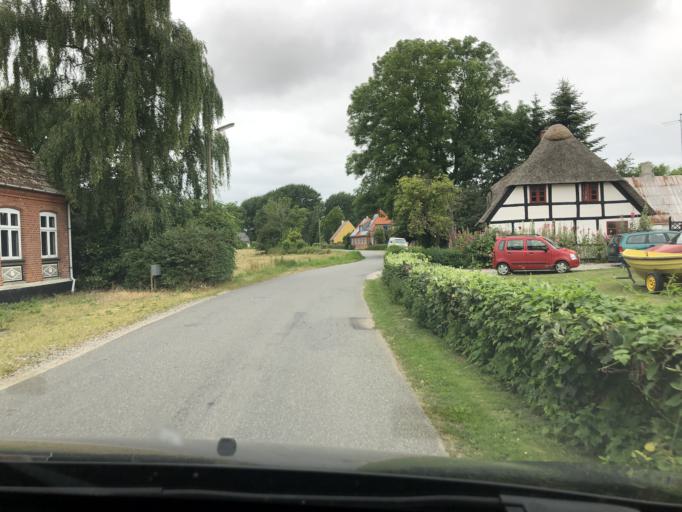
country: DK
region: South Denmark
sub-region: AEro Kommune
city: AEroskobing
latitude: 54.9140
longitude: 10.2978
